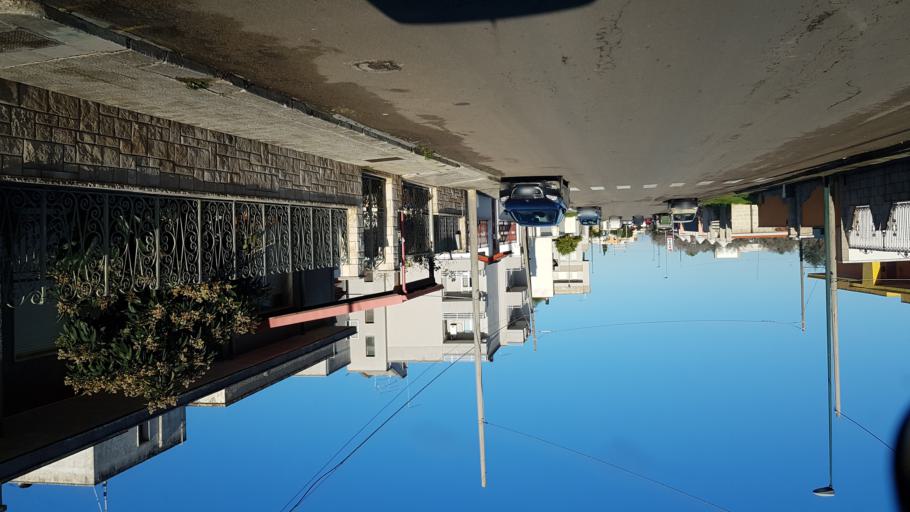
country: IT
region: Apulia
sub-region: Provincia di Brindisi
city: Torchiarolo
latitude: 40.4832
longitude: 18.0494
